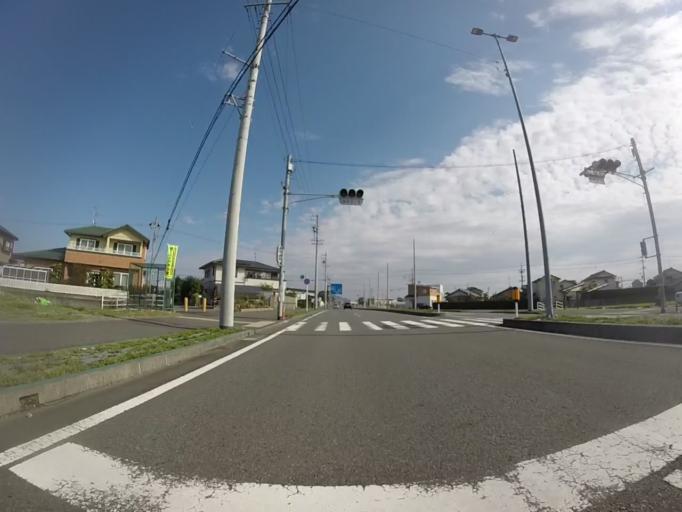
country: JP
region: Shizuoka
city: Fujieda
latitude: 34.8277
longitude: 138.2670
